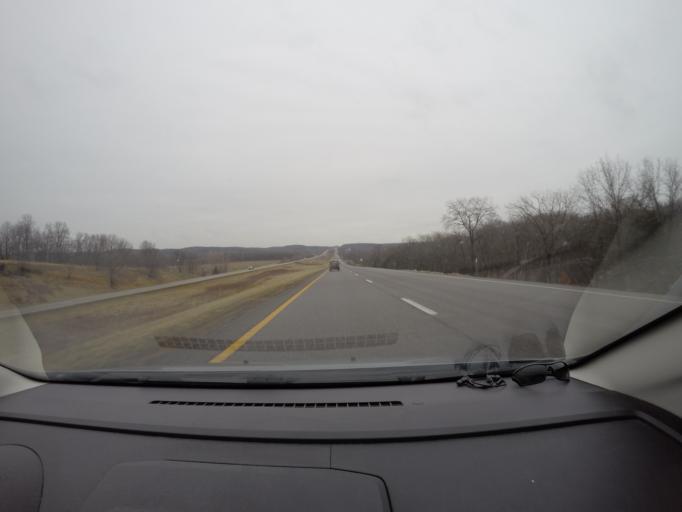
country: US
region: Missouri
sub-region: Montgomery County
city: Montgomery City
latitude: 38.8980
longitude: -91.5950
